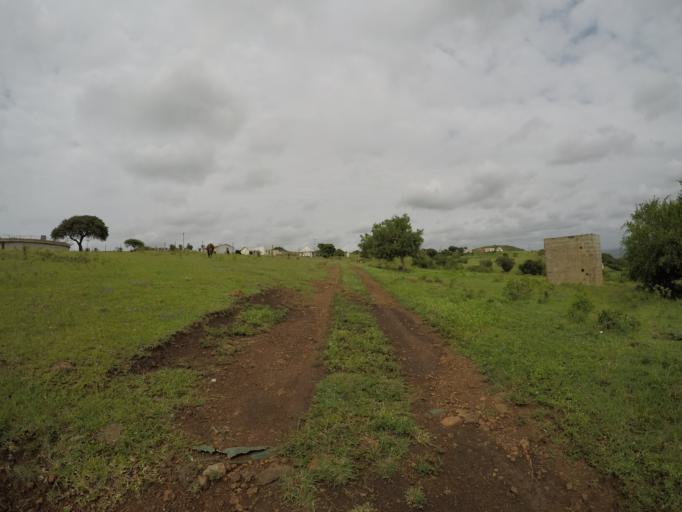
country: ZA
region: KwaZulu-Natal
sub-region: uThungulu District Municipality
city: Empangeni
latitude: -28.6149
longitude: 31.8985
